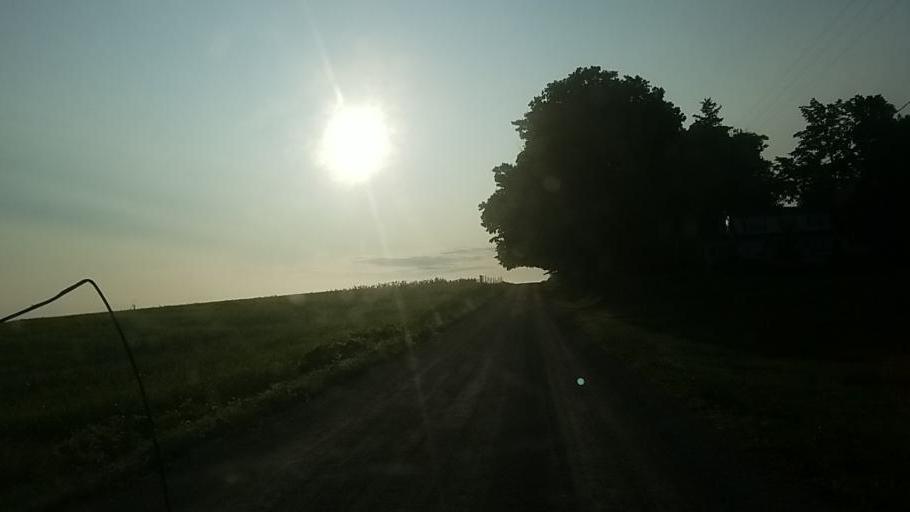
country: US
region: Michigan
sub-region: Newaygo County
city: Fremont
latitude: 43.4529
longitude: -86.0306
